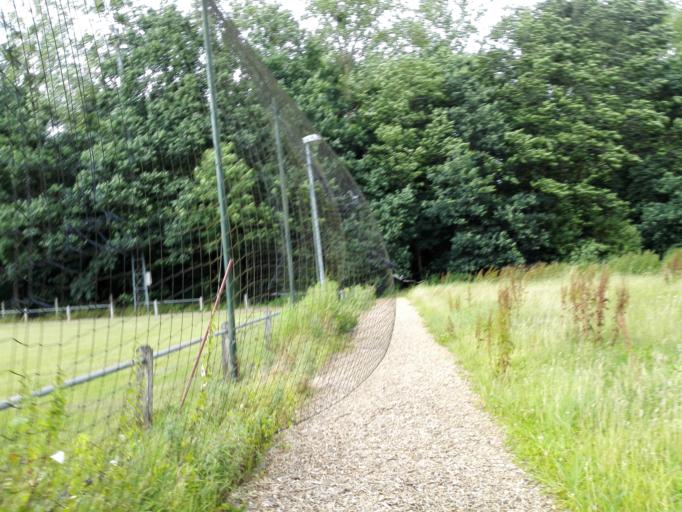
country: BE
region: Flanders
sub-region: Provincie Vlaams-Brabant
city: Bierbeek
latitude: 50.8548
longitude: 4.7649
